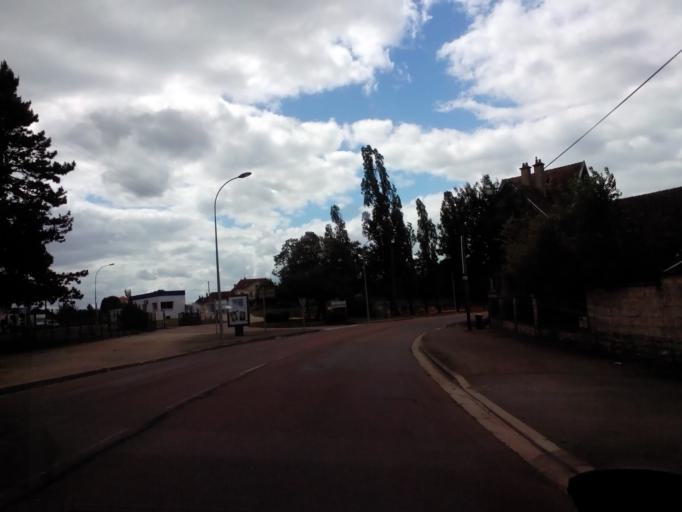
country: FR
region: Bourgogne
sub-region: Departement de la Cote-d'Or
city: Chatillon-sur-Seine
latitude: 47.8721
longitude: 4.5707
